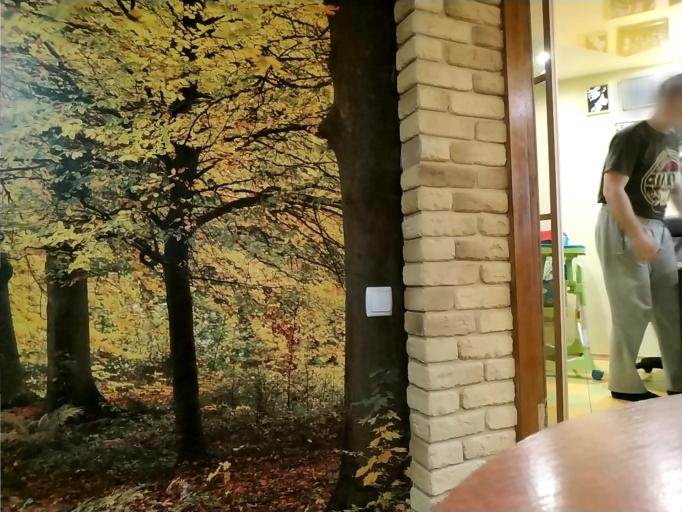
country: RU
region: Tverskaya
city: Staraya Toropa
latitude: 56.3394
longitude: 31.8565
